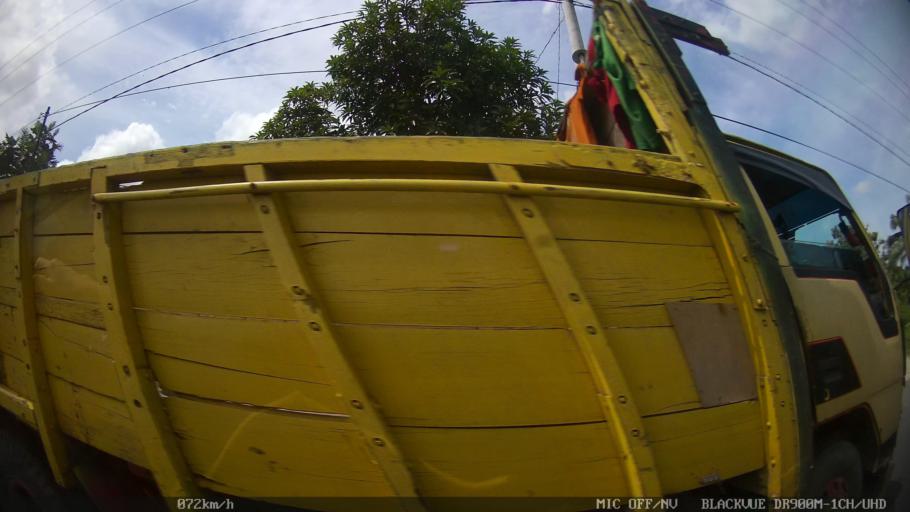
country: ID
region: North Sumatra
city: Percut
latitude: 3.5893
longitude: 98.8670
